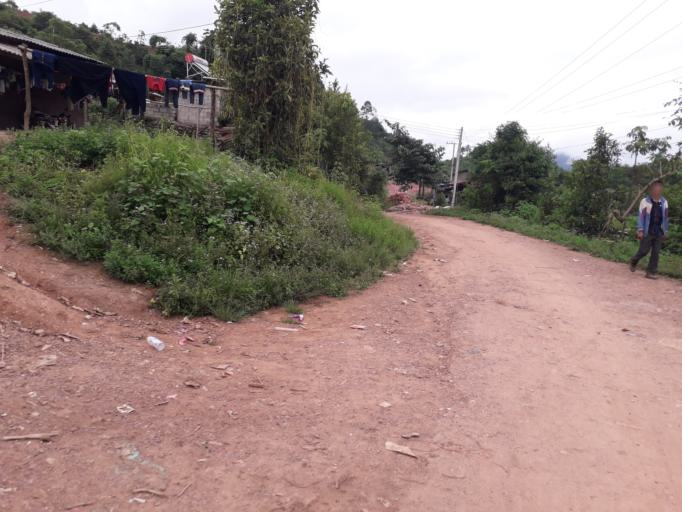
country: CN
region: Yunnan
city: Menglie
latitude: 22.2479
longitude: 101.6073
